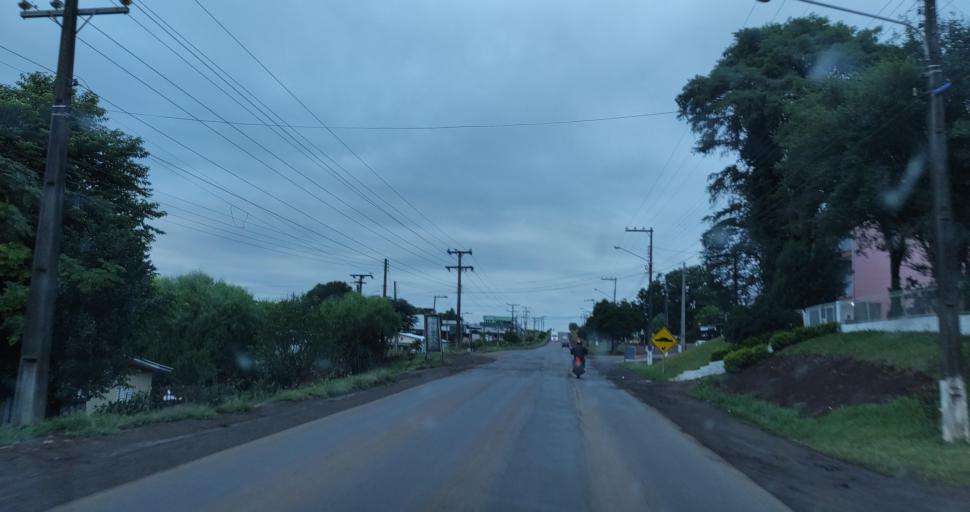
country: BR
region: Santa Catarina
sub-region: Xanxere
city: Xanxere
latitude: -26.7368
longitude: -52.3931
